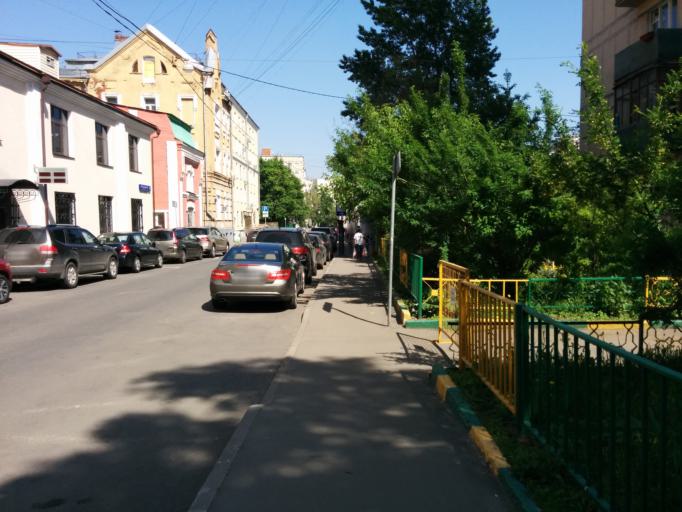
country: RU
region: Moscow
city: Zamoskvorech'ye
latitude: 55.7321
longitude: 37.6297
